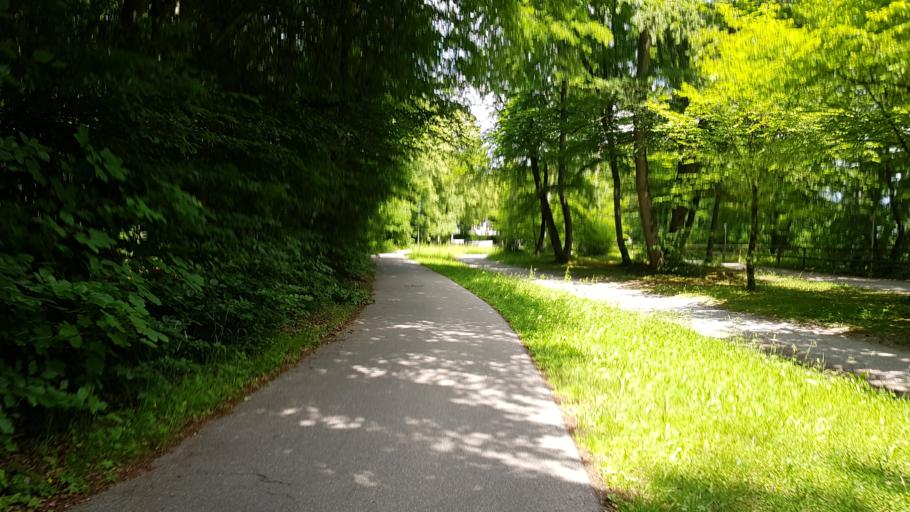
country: DE
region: Bavaria
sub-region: Upper Bavaria
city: Grunwald
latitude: 48.0469
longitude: 11.5146
